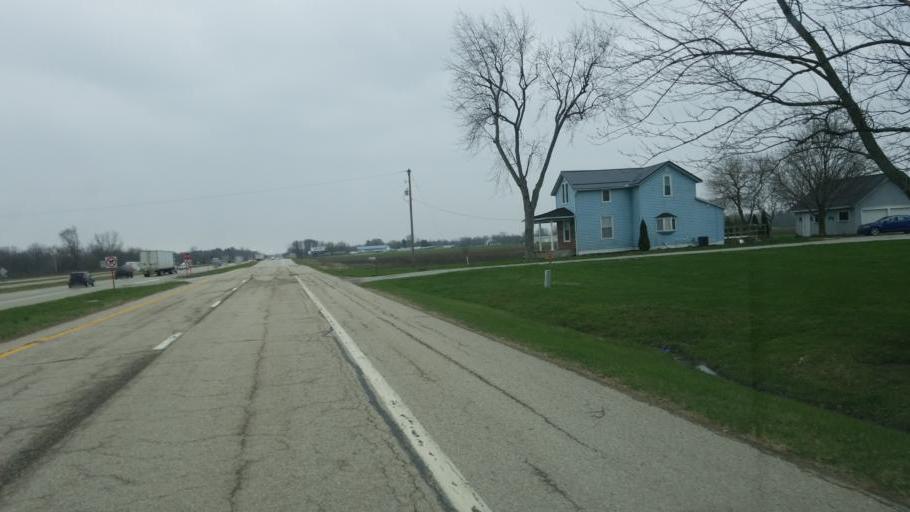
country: US
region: Ohio
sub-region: Delaware County
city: Delaware
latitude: 40.3882
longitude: -83.0743
